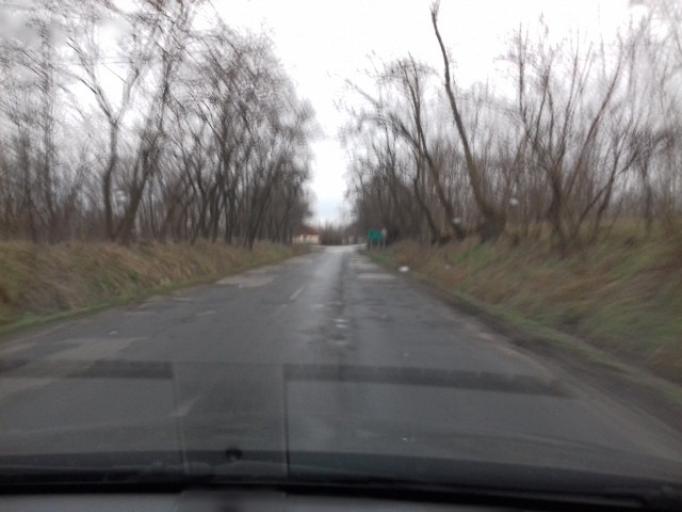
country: HU
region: Szabolcs-Szatmar-Bereg
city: Nyirbogdany
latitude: 48.0657
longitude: 21.8606
